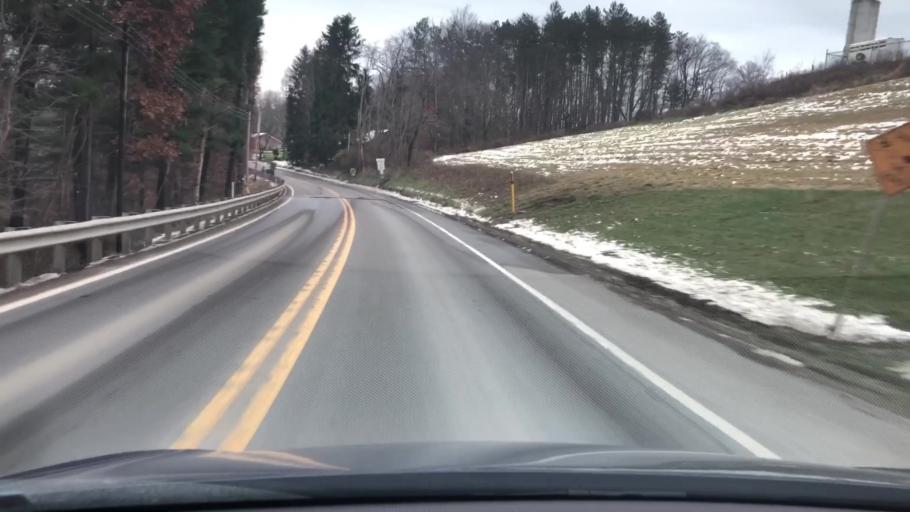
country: US
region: Pennsylvania
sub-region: Clarion County
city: Clarion
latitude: 41.0308
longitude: -79.2645
